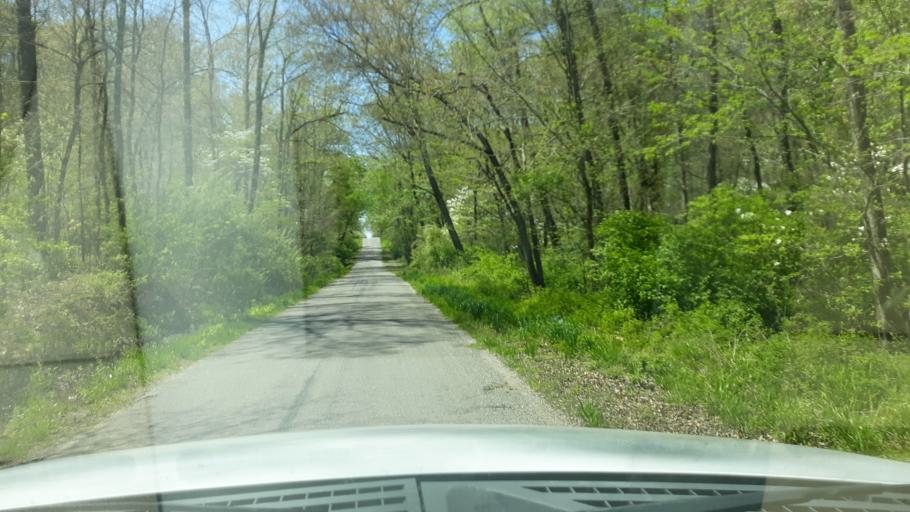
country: US
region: Illinois
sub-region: Saline County
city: Harrisburg
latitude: 37.8596
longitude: -88.6284
